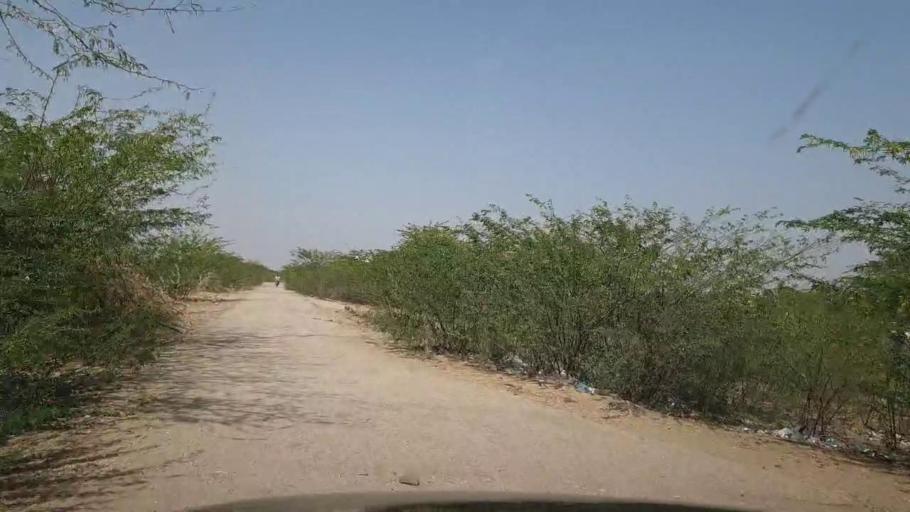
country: PK
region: Sindh
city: Islamkot
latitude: 25.0614
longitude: 70.4497
